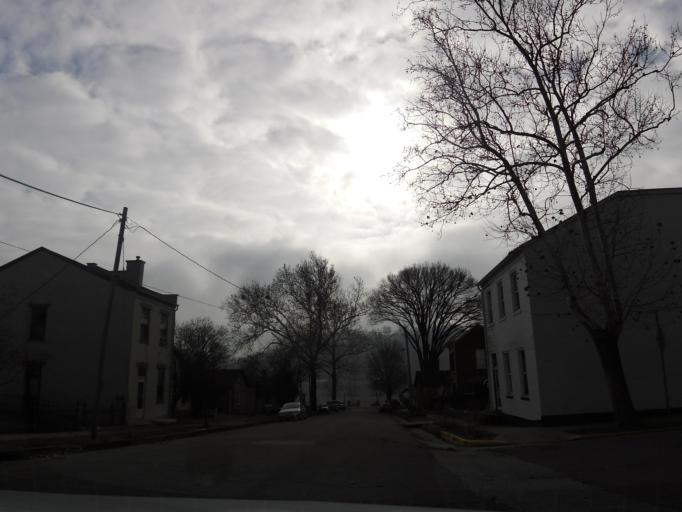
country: US
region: Indiana
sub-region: Jefferson County
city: Madison
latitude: 38.7339
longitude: -85.3743
